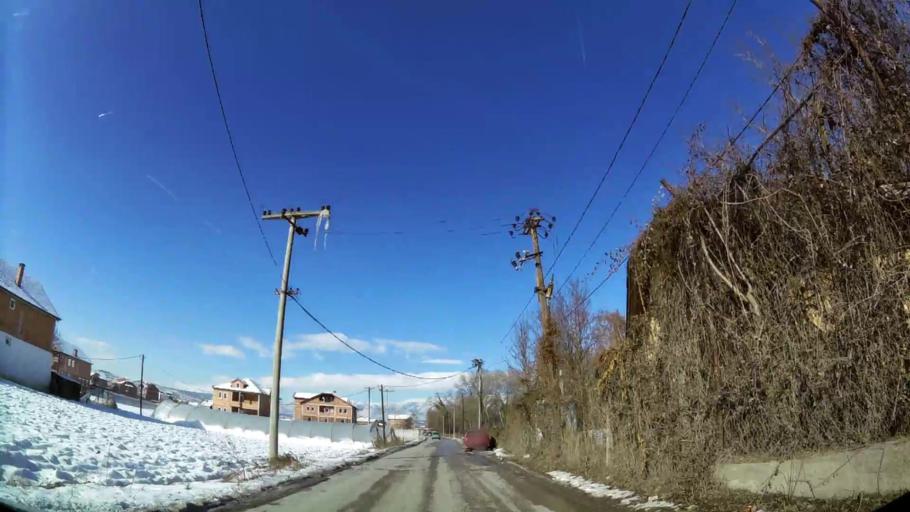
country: MK
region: Saraj
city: Saraj
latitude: 41.9993
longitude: 21.3407
